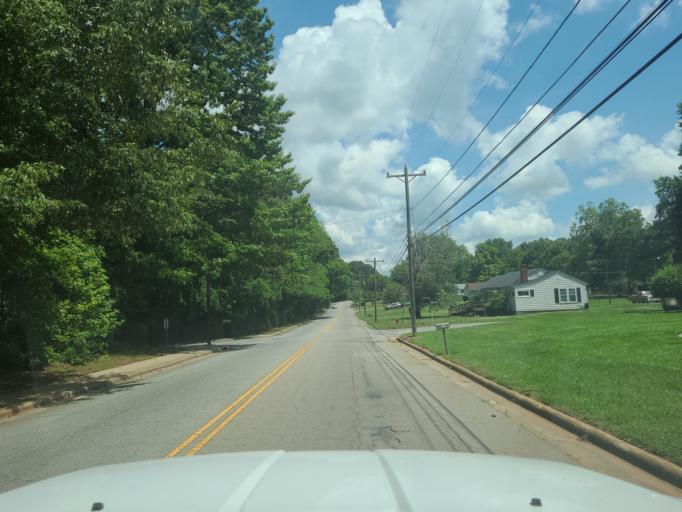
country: US
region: North Carolina
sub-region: Rowan County
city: East Spencer
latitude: 35.6887
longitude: -80.4213
